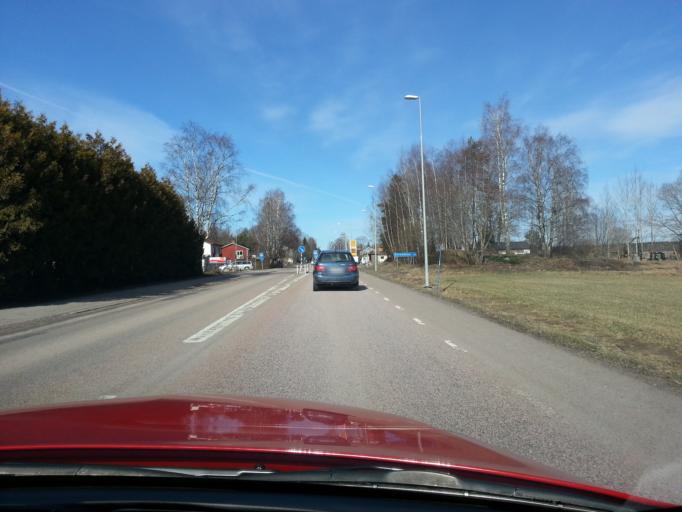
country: SE
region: Uppsala
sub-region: Osthammars Kommun
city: Gimo
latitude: 60.1667
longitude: 18.1936
